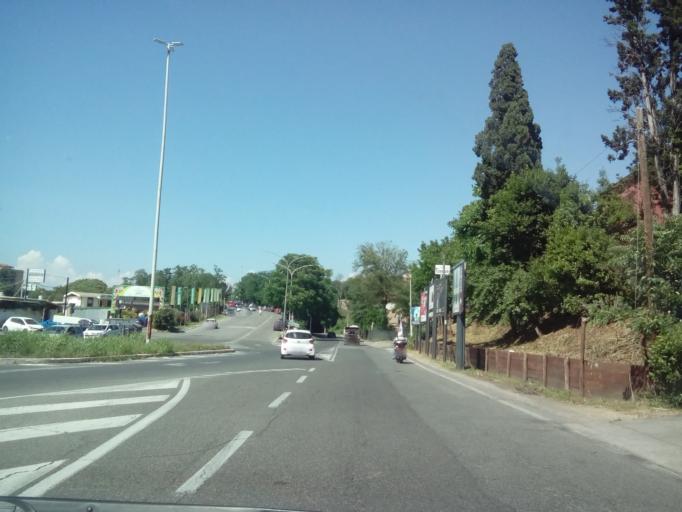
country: IT
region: Latium
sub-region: Citta metropolitana di Roma Capitale
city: Rome
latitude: 41.8466
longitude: 12.4733
